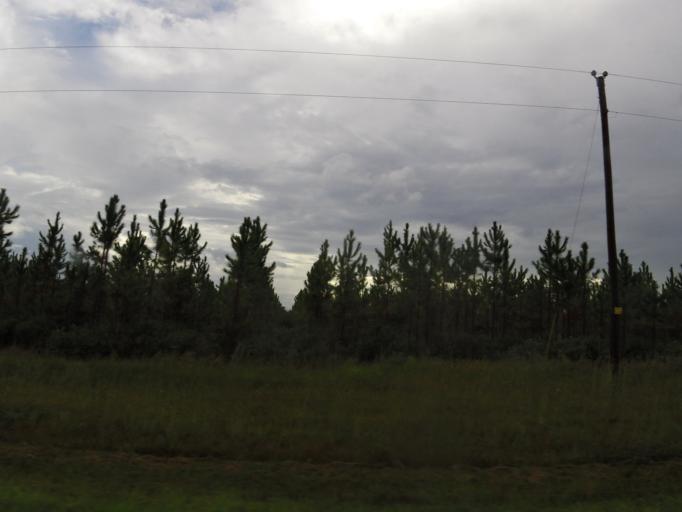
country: US
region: Florida
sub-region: Duval County
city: Baldwin
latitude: 30.3991
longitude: -82.0048
